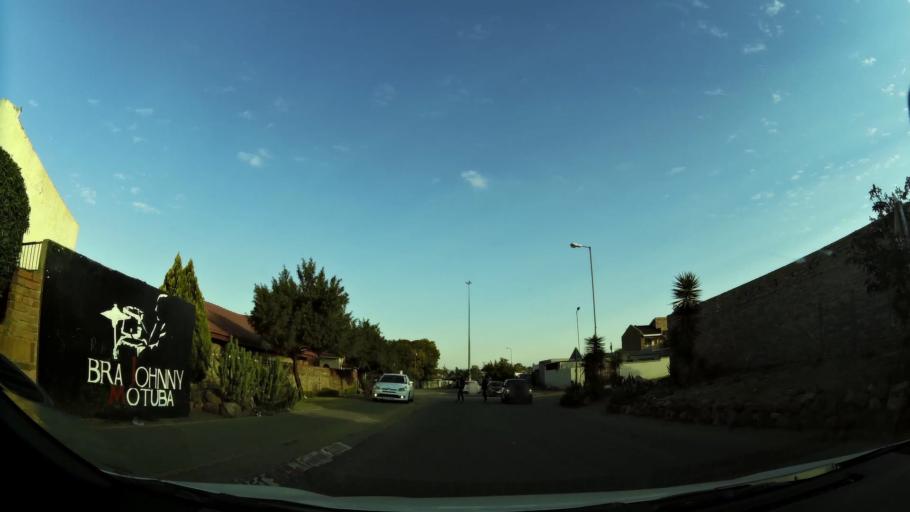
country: ZA
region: Gauteng
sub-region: City of Tshwane Metropolitan Municipality
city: Cullinan
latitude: -25.7146
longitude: 28.3613
